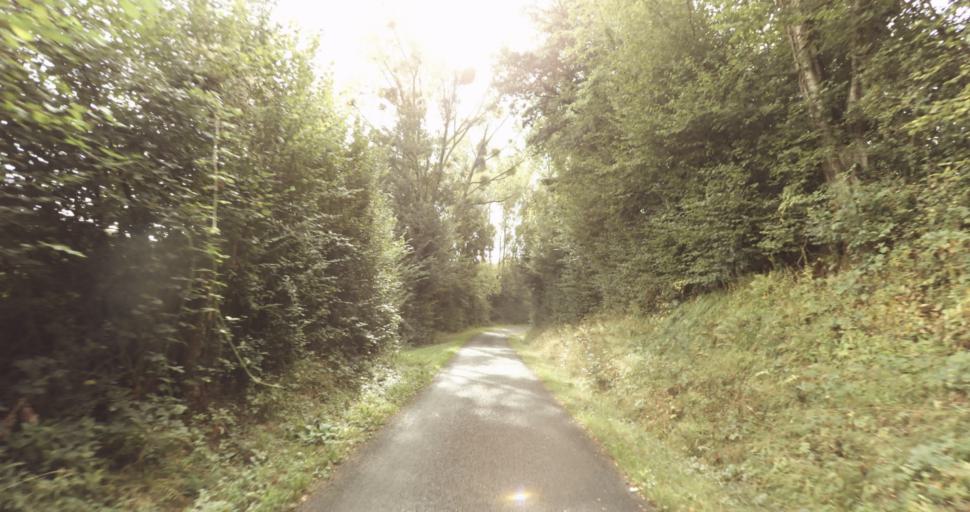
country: FR
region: Lower Normandy
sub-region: Departement de l'Orne
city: Gace
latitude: 48.8405
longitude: 0.3060
